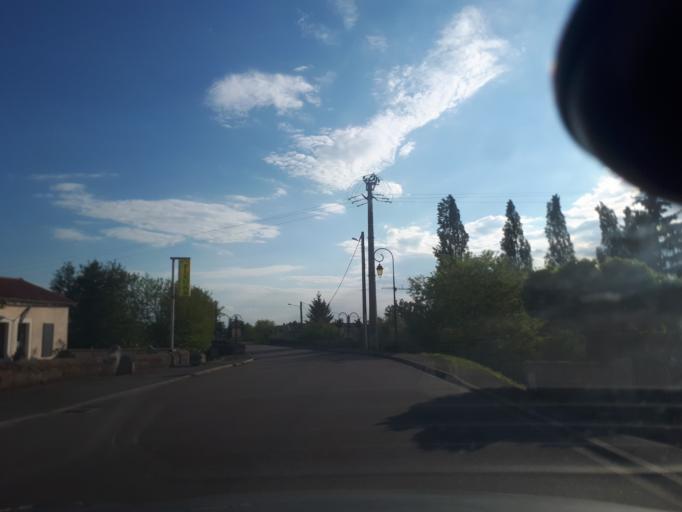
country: FR
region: Bourgogne
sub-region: Departement de Saone-et-Loire
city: Saint-Yan
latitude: 46.4106
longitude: 4.0355
